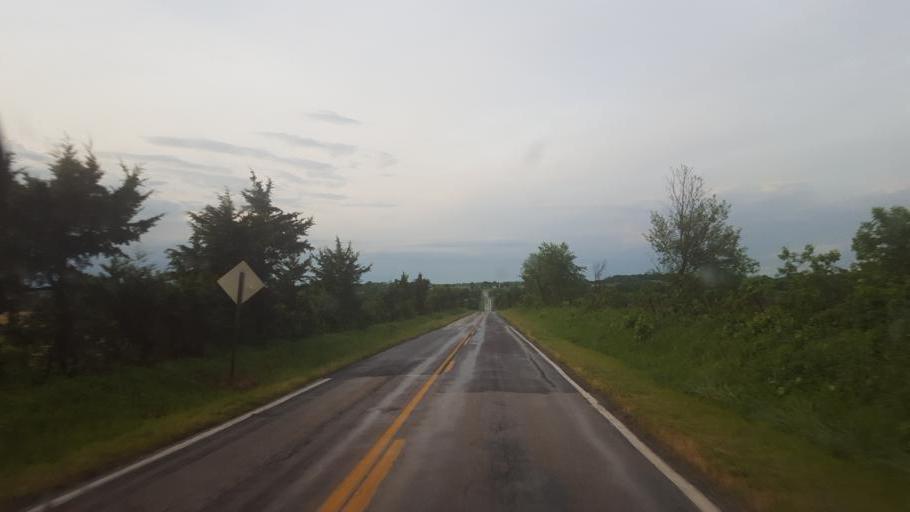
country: US
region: Missouri
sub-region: Moniteau County
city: California
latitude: 38.7088
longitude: -92.6345
